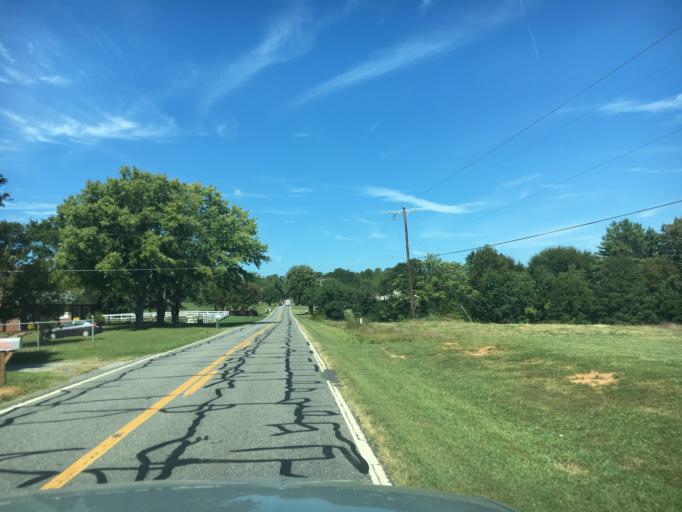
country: US
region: North Carolina
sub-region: Rutherford County
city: Spindale
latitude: 35.2916
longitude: -81.9365
